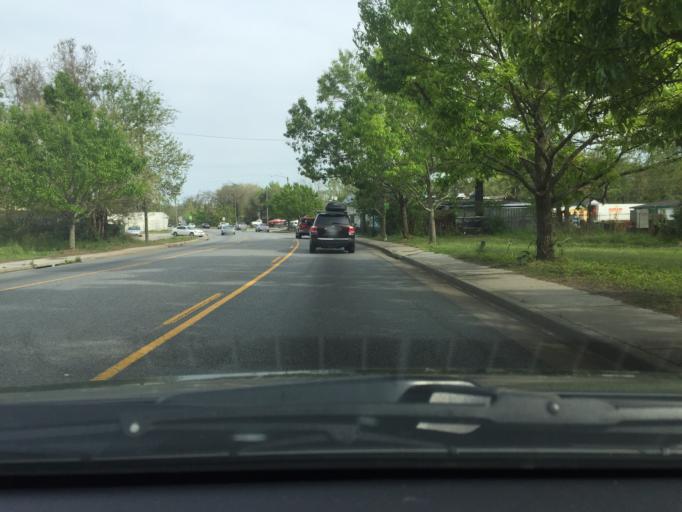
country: US
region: Georgia
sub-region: Chatham County
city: Savannah
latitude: 32.0625
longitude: -81.0772
